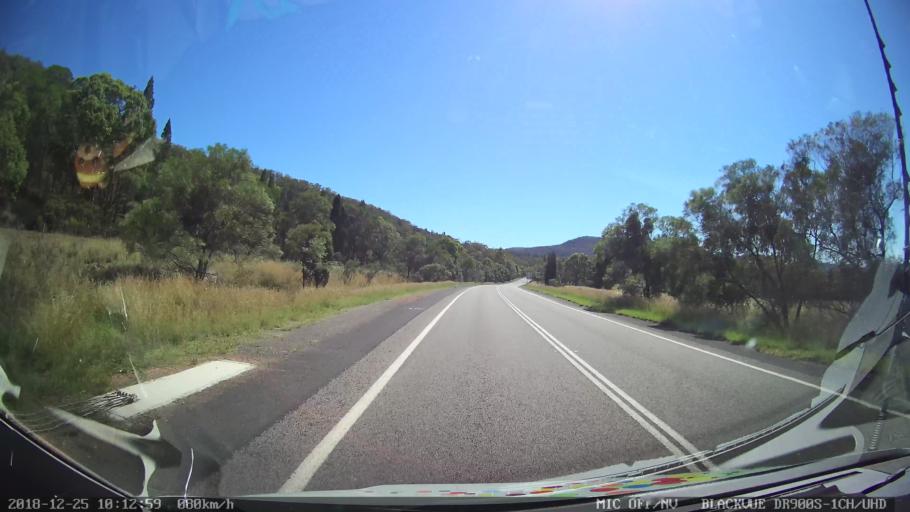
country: AU
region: New South Wales
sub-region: Muswellbrook
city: Denman
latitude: -32.3269
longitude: 150.5381
